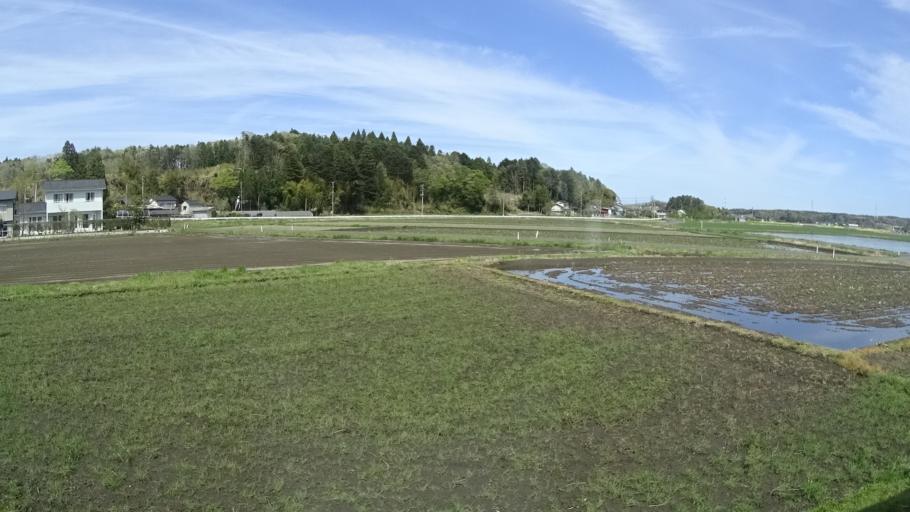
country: JP
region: Fukushima
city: Namie
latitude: 37.6091
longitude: 140.9867
